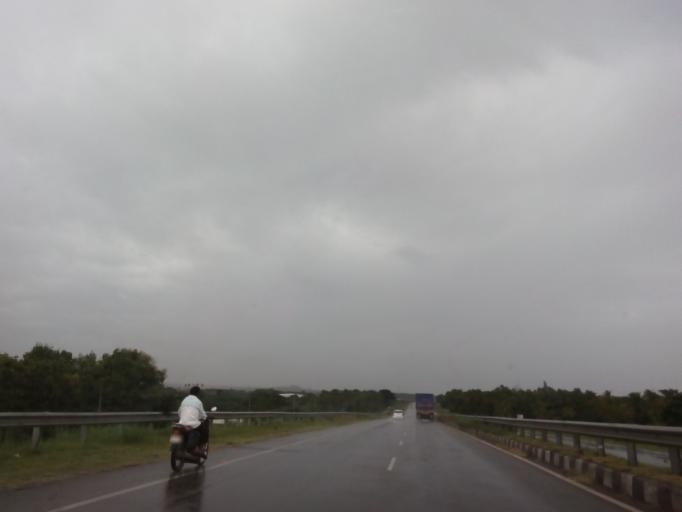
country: IN
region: Karnataka
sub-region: Davanagere
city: Harihar
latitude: 14.4339
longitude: 75.9618
